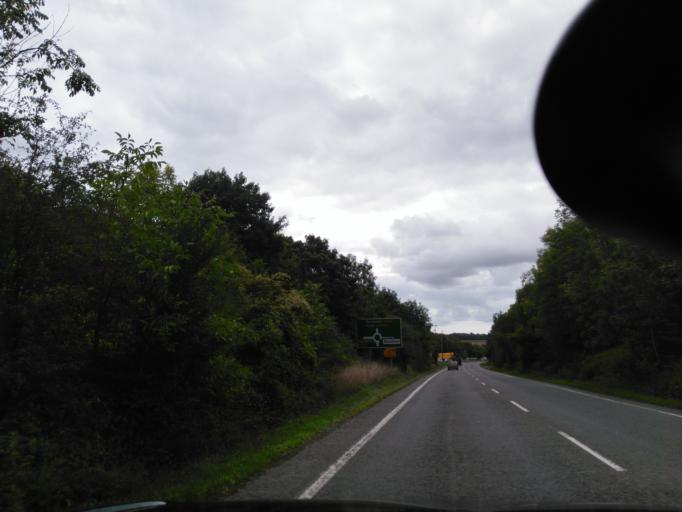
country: GB
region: England
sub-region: Dorset
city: Blandford Forum
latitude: 50.8707
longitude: -2.1511
